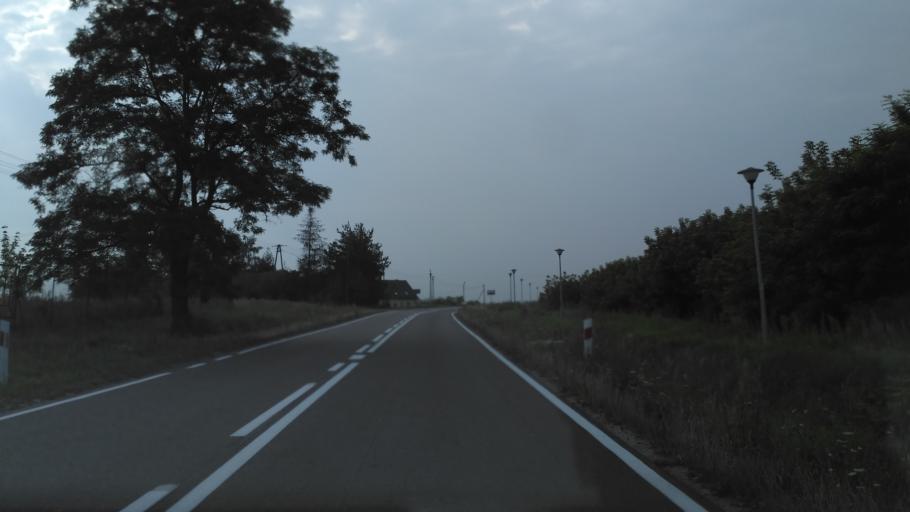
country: PL
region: Lublin Voivodeship
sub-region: Powiat chelmski
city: Rejowiec Fabryczny
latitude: 51.1855
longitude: 23.1711
